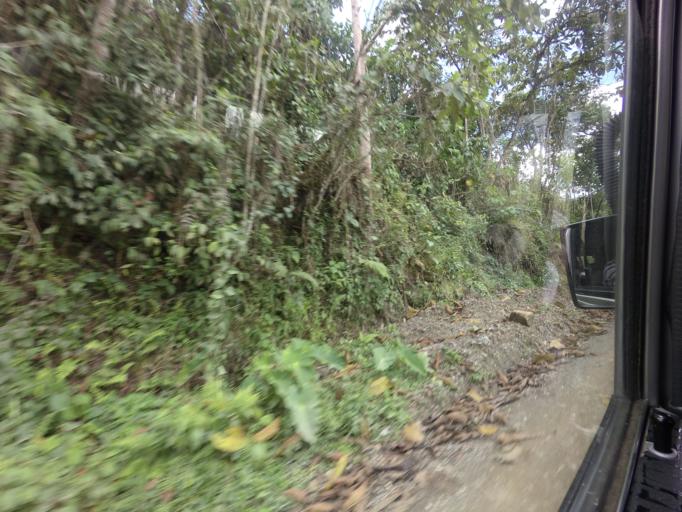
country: CO
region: Huila
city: Isnos
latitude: 1.9557
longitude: -76.2800
